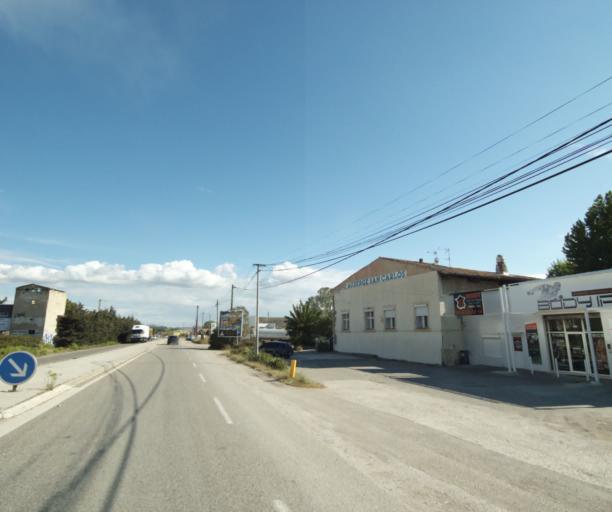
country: FR
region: Provence-Alpes-Cote d'Azur
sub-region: Departement des Bouches-du-Rhone
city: Rognac
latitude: 43.4898
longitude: 5.2194
